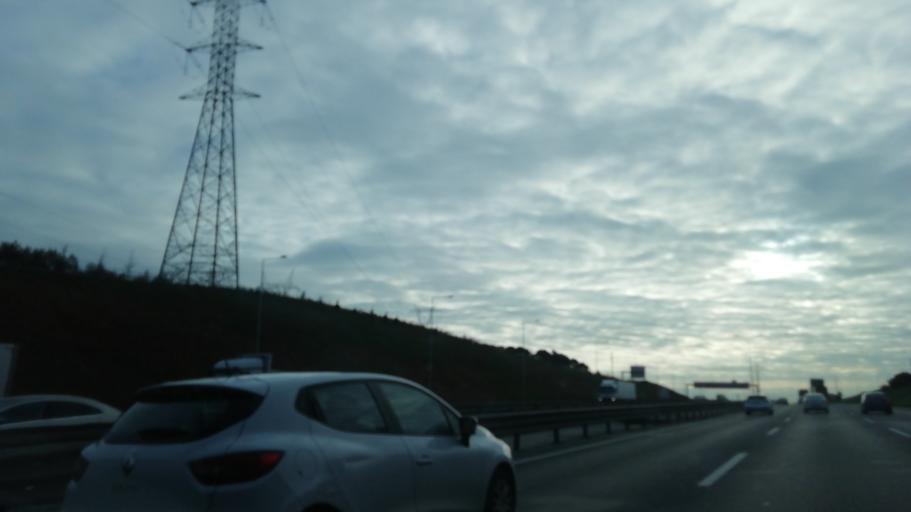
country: TR
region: Istanbul
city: Sultanbeyli
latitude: 40.9464
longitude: 29.3115
